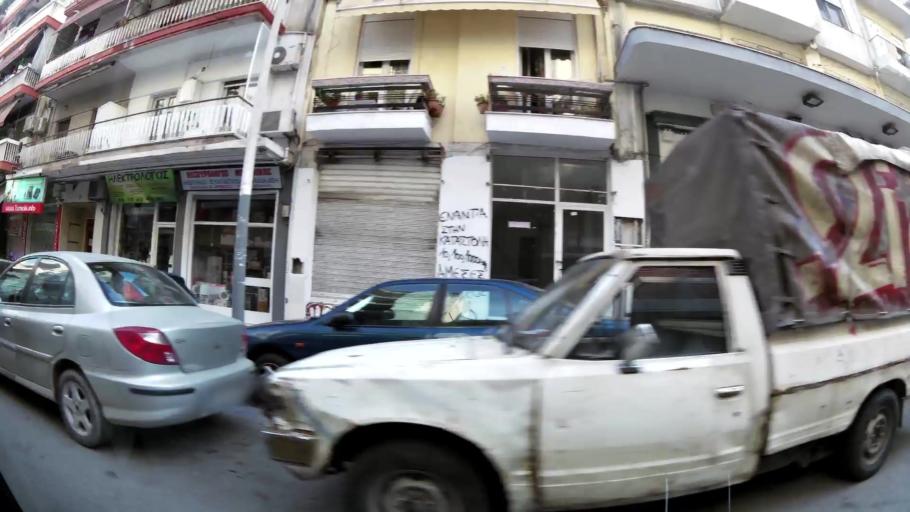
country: GR
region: Central Macedonia
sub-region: Nomos Thessalonikis
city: Sykies
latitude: 40.6403
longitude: 22.9465
